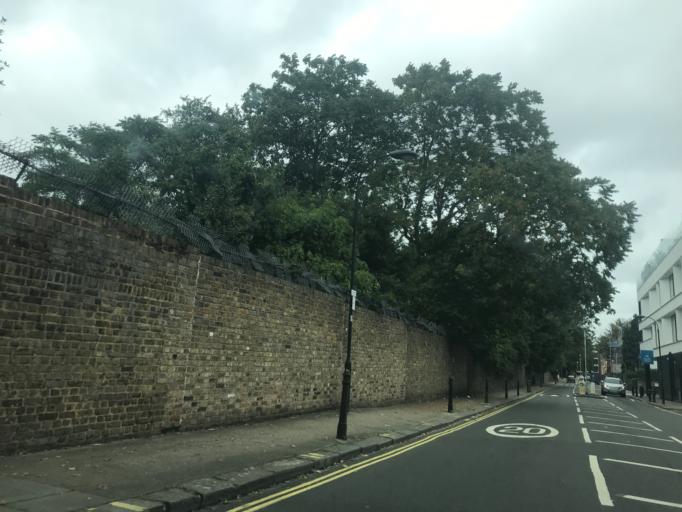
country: GB
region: England
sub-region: Greater London
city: Wandsworth
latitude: 51.4655
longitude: -0.1973
